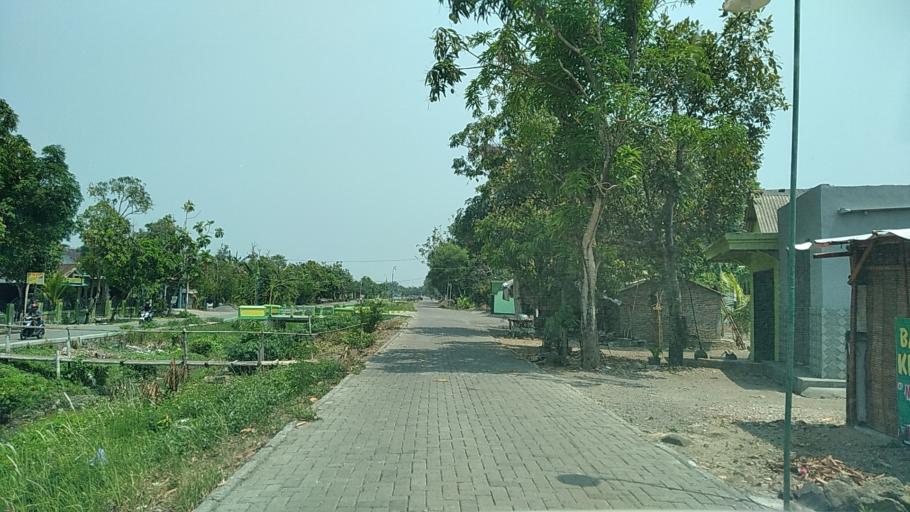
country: ID
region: Central Java
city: Mranggen
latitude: -7.0311
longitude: 110.4814
